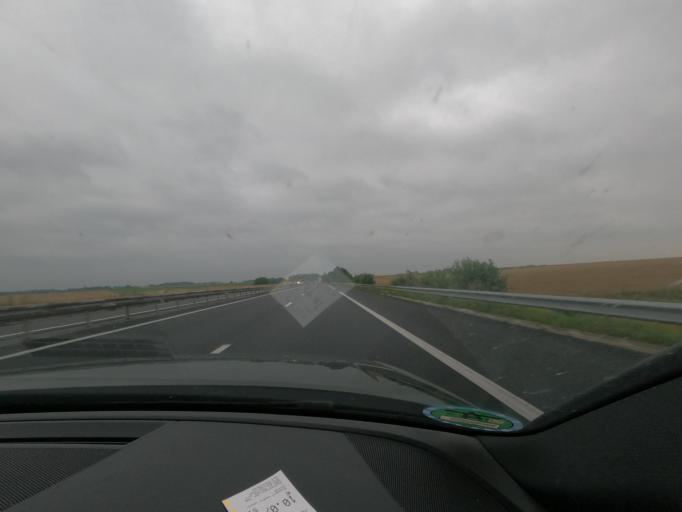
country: FR
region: Picardie
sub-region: Departement de la Somme
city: Moislains
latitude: 50.0592
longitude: 2.9562
